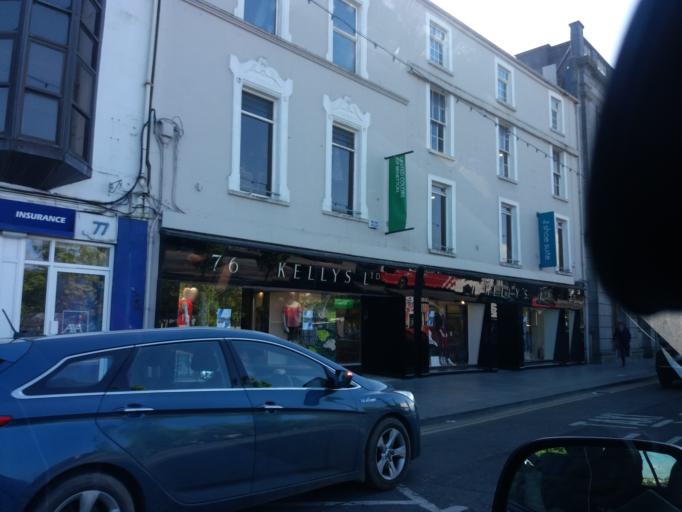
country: IE
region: Munster
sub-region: Waterford
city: Waterford
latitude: 52.2619
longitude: -7.1108
